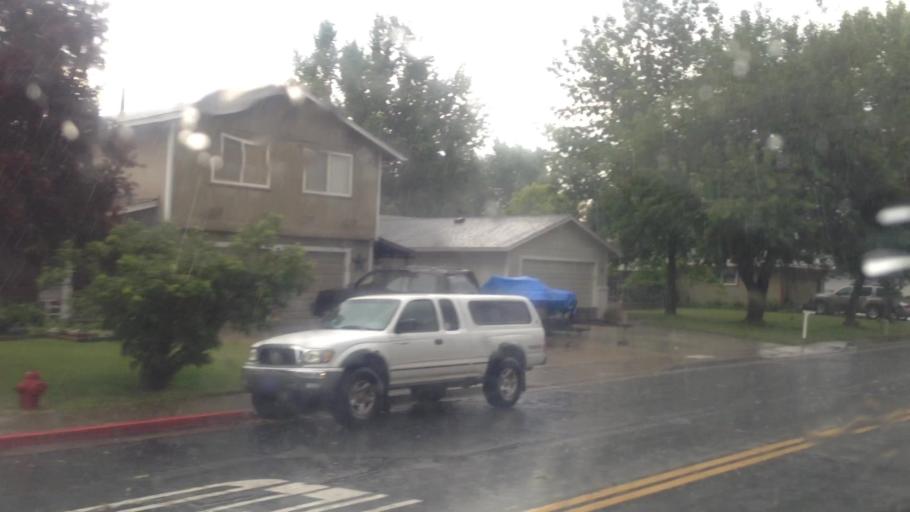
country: US
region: Nevada
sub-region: Washoe County
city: Sparks
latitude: 39.4893
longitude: -119.7488
